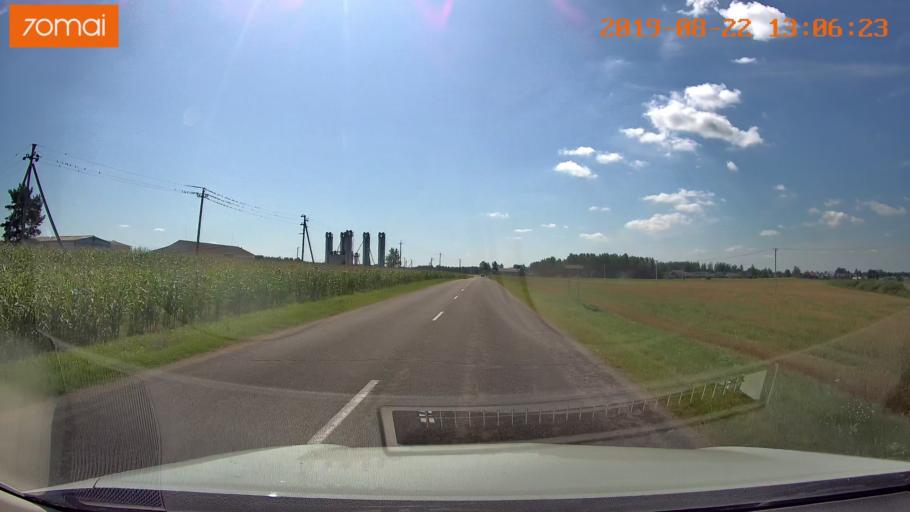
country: BY
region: Minsk
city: Prawdzinski
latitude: 53.3477
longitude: 27.8387
